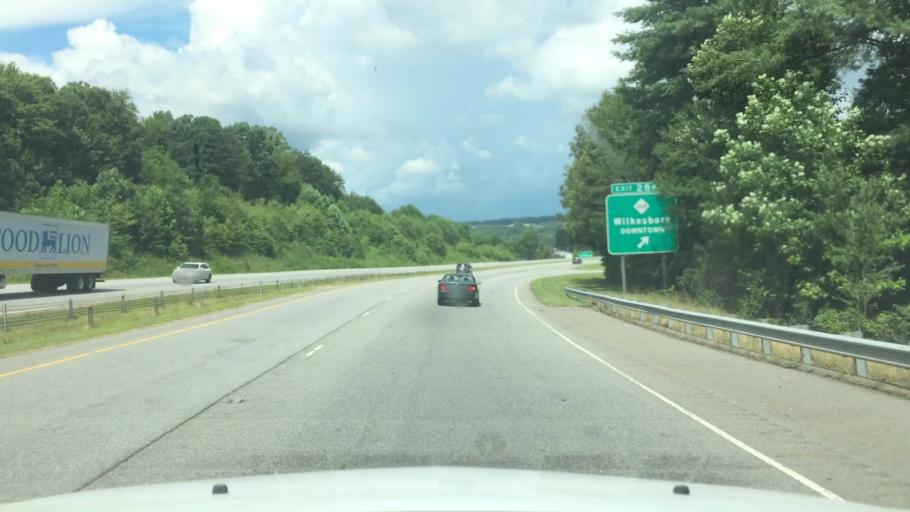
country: US
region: North Carolina
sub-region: Wilkes County
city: Wilkesboro
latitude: 36.1386
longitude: -81.1697
